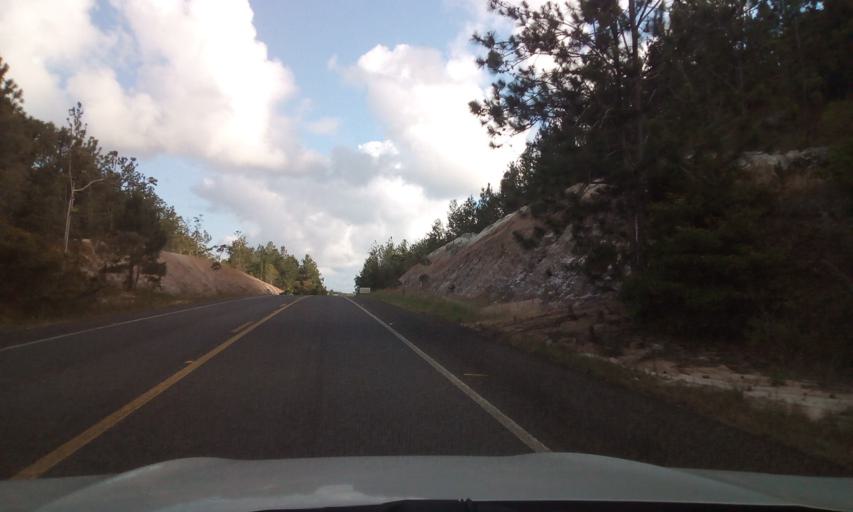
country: BR
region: Bahia
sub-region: Entre Rios
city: Entre Rios
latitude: -12.1150
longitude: -37.7867
